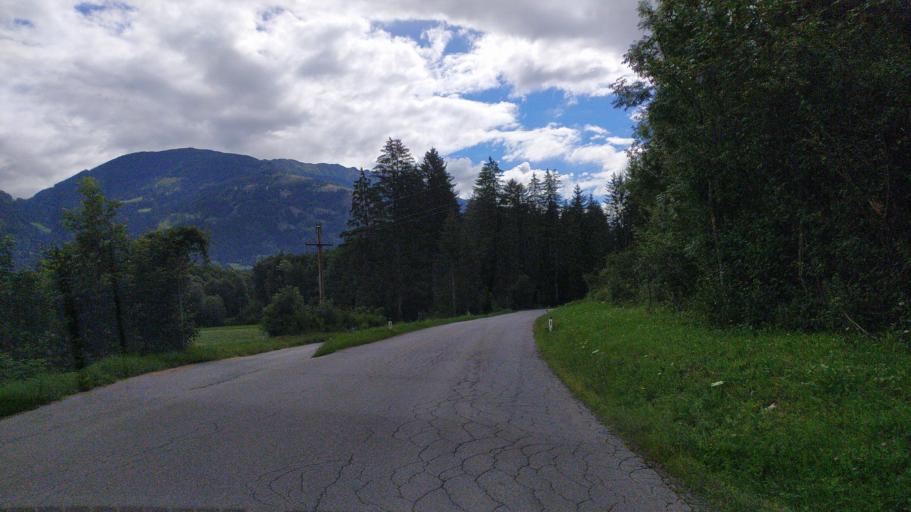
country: AT
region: Tyrol
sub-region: Politischer Bezirk Lienz
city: Tristach
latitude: 46.8141
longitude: 12.8128
